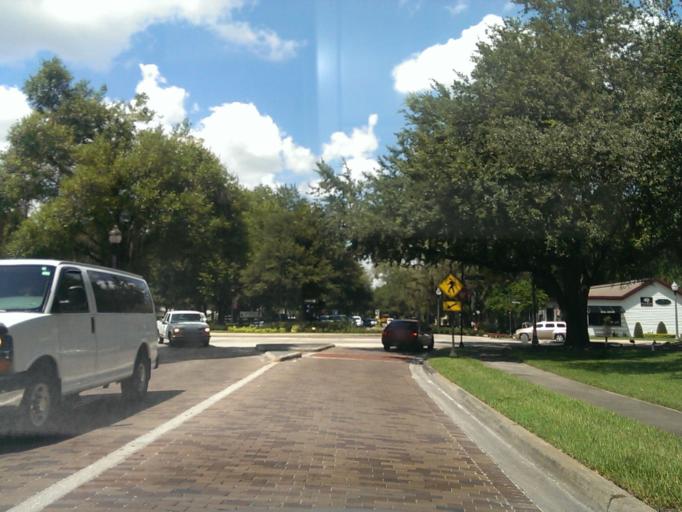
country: US
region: Florida
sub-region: Orange County
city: Windermere
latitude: 28.4941
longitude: -81.5343
